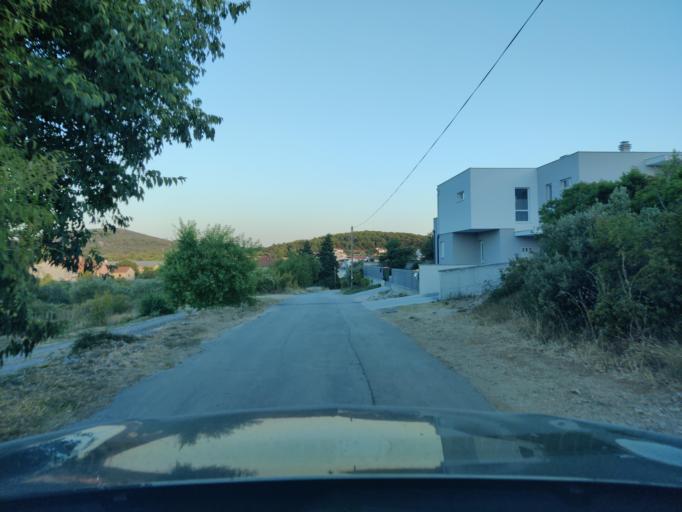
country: HR
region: Sibensko-Kniniska
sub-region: Grad Sibenik
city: Tisno
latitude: 43.8050
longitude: 15.6468
